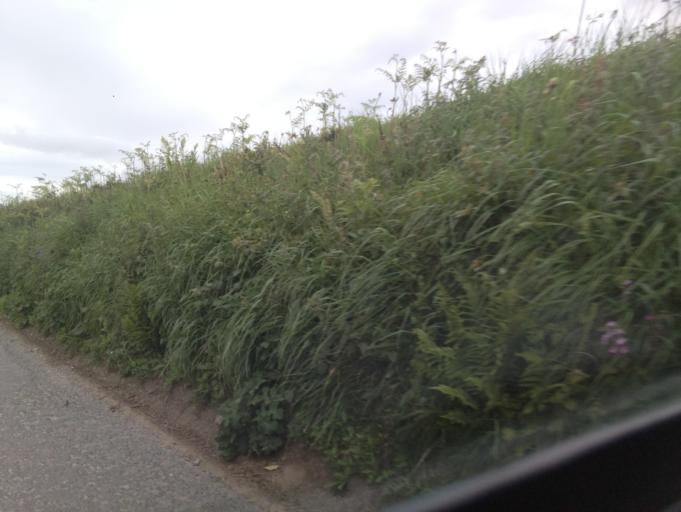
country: GB
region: England
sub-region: Devon
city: Dartmouth
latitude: 50.3279
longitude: -3.6423
